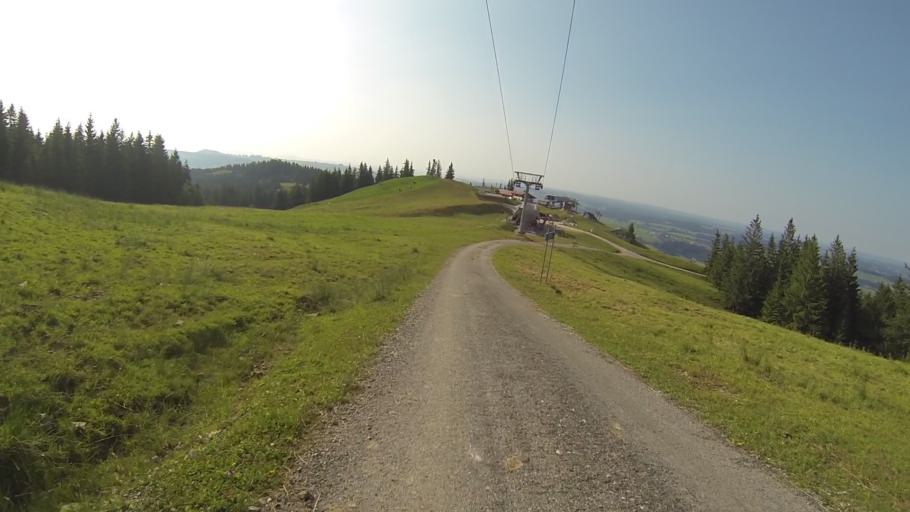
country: DE
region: Bavaria
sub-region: Swabia
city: Nesselwang
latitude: 47.6045
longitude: 10.4983
